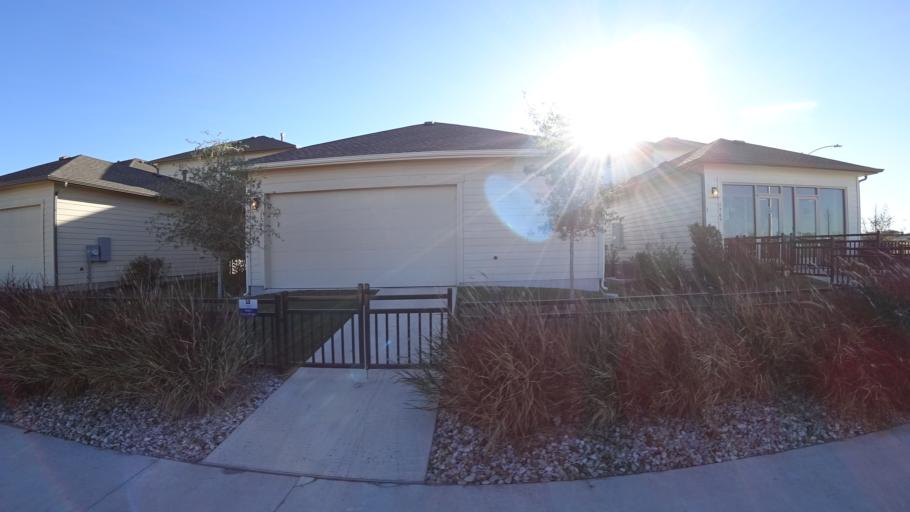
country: US
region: Texas
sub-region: Travis County
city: Austin
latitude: 30.2242
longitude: -97.6982
